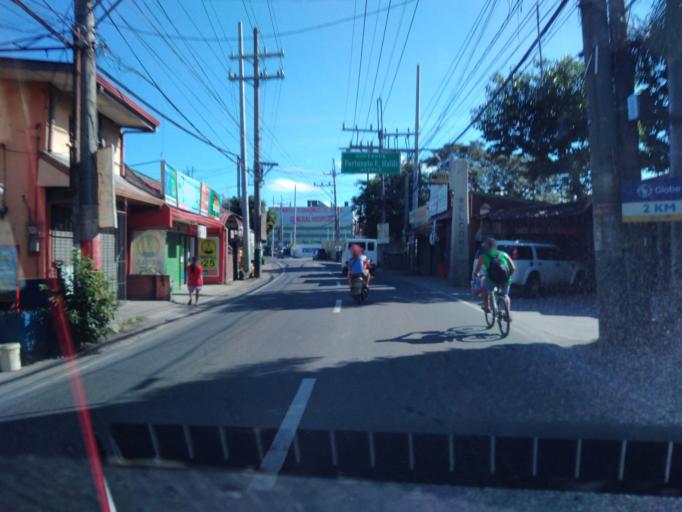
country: PH
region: Central Luzon
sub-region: Province of Bulacan
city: Santa Maria
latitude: 14.8086
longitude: 120.9463
